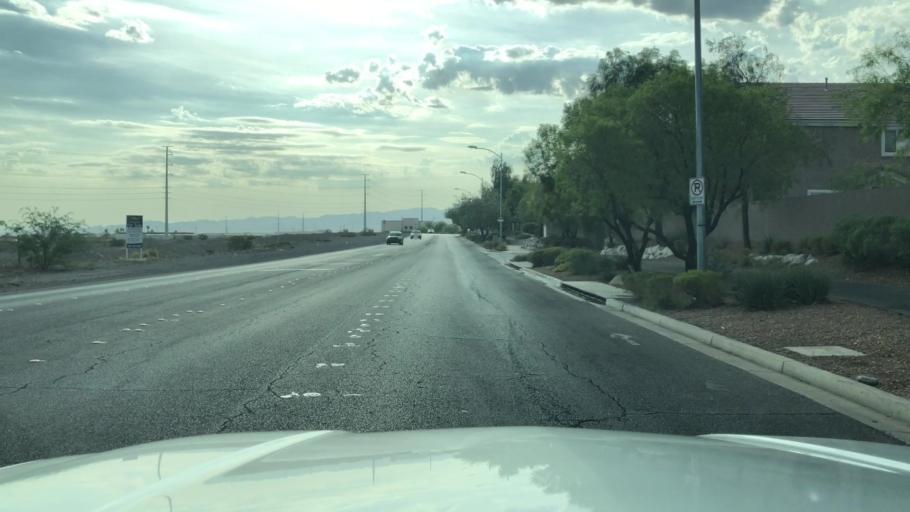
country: US
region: Nevada
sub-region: Clark County
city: Whitney
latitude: 36.0344
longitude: -115.0428
